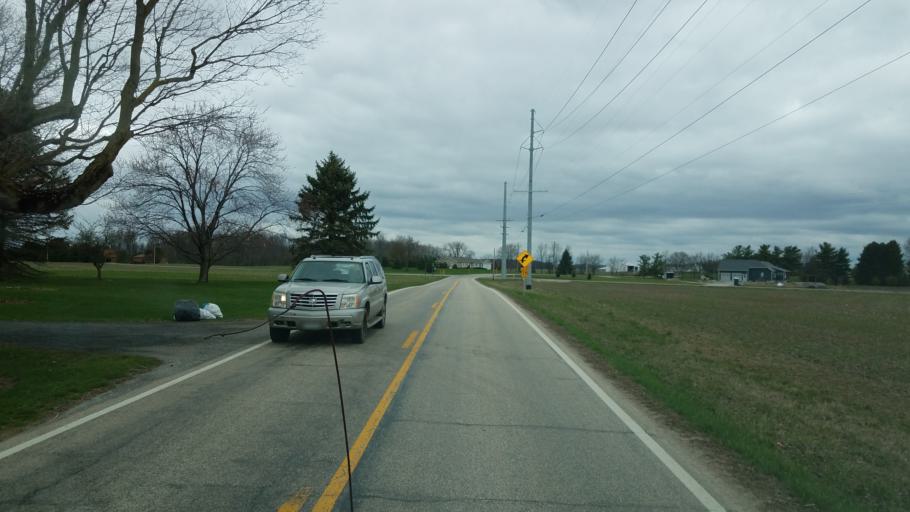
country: US
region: Ohio
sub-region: Delaware County
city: Delaware
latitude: 40.3641
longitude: -83.1017
